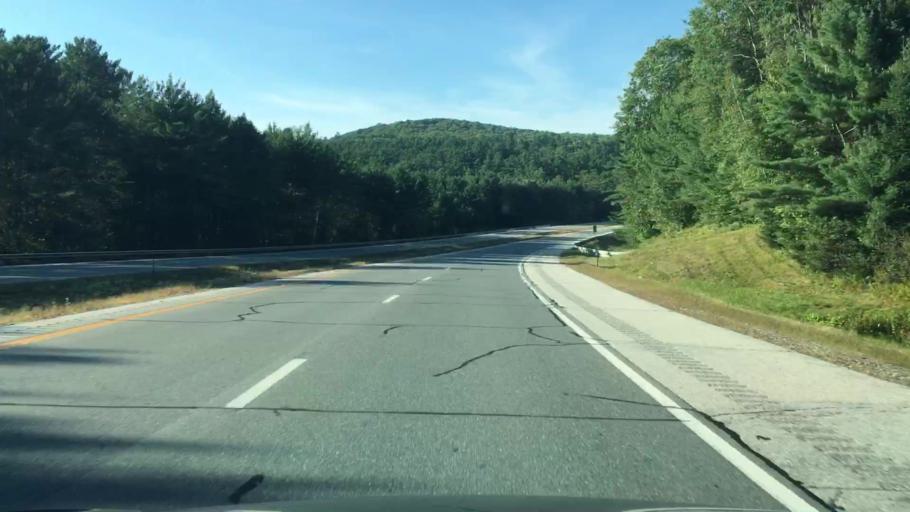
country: US
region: New Hampshire
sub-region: Grafton County
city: Littleton
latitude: 44.2456
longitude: -71.7605
